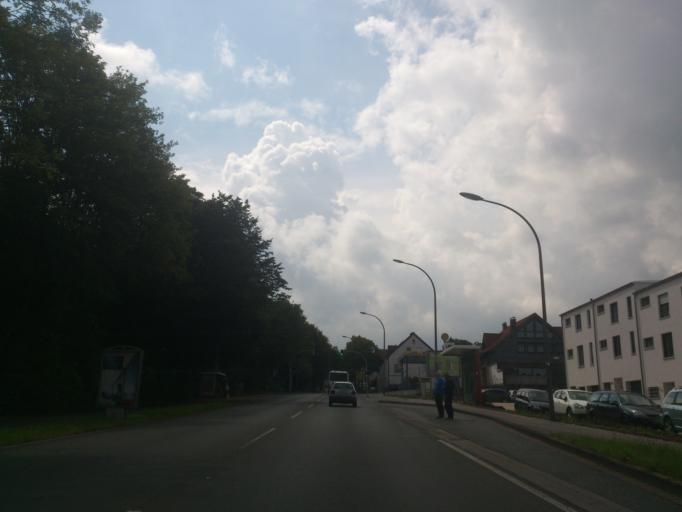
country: DE
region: North Rhine-Westphalia
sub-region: Regierungsbezirk Arnsberg
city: Dortmund
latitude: 51.4814
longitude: 7.4155
